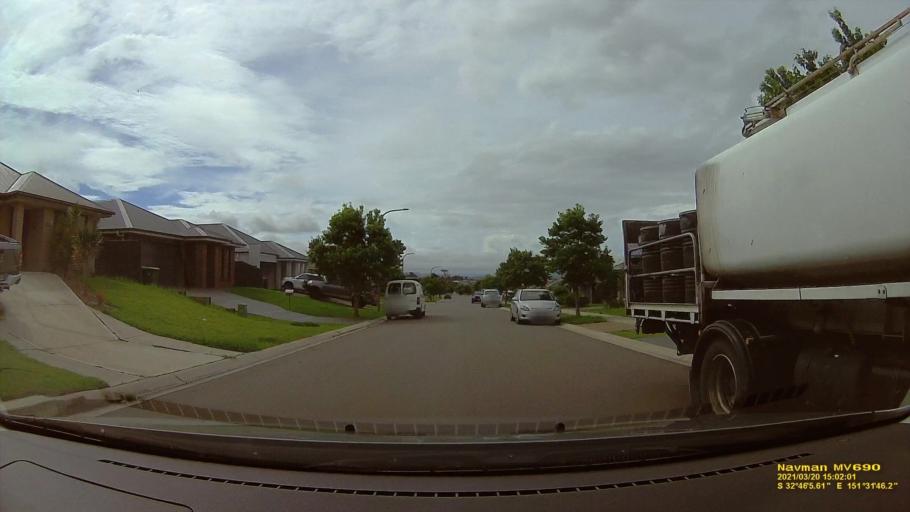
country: AU
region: New South Wales
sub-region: Cessnock
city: Heddon Greta
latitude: -32.7681
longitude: 151.5295
